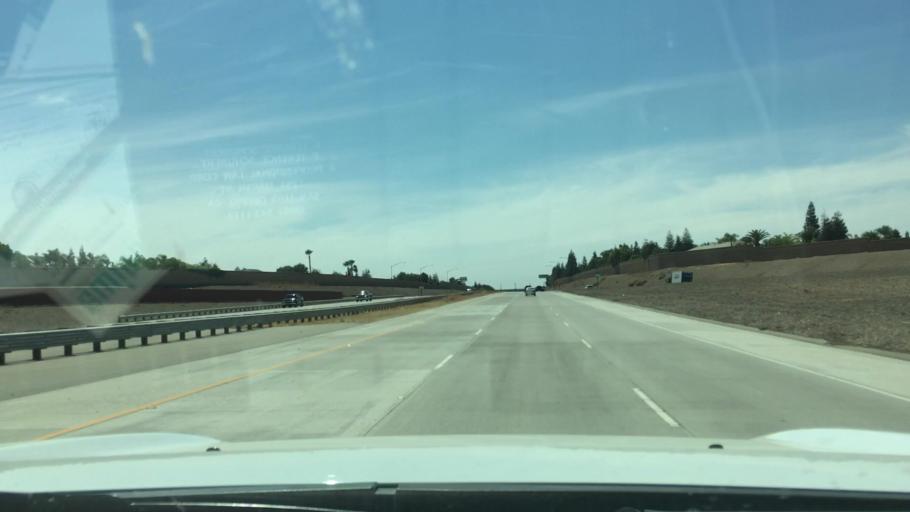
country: US
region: California
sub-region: Kern County
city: Greenacres
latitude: 35.3621
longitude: -119.1166
